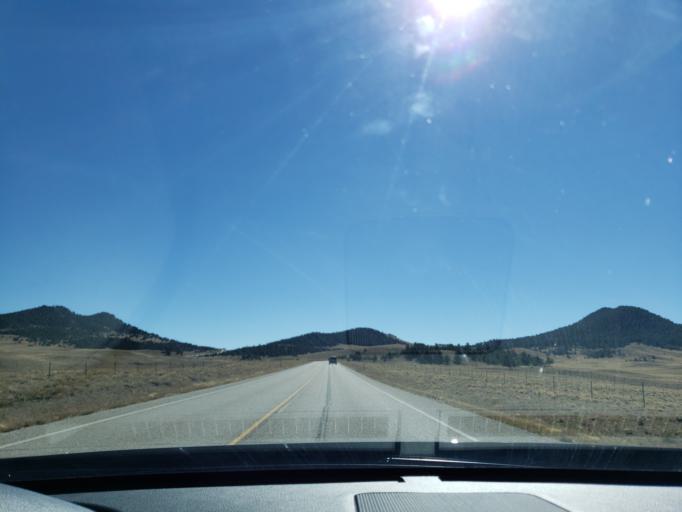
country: US
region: Colorado
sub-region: Chaffee County
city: Salida
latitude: 38.8526
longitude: -105.6524
